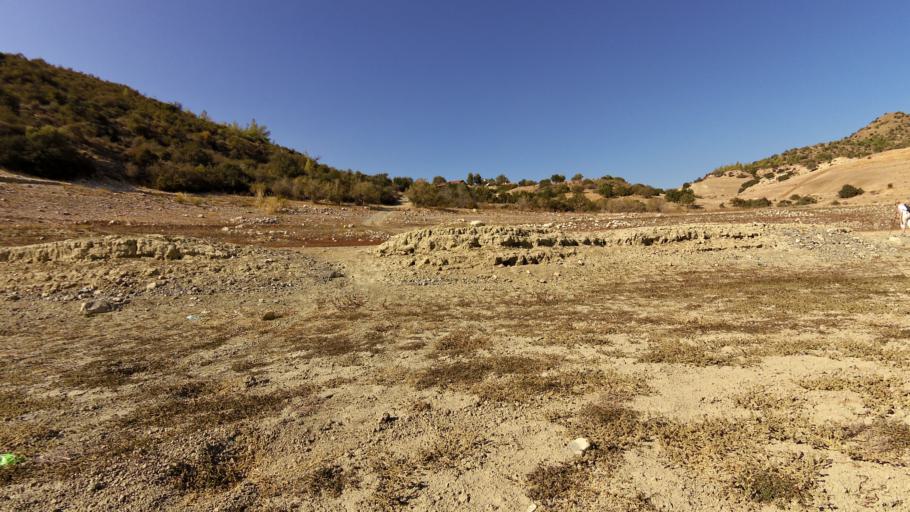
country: CY
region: Limassol
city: Mouttagiaka
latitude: 34.7585
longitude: 33.0915
